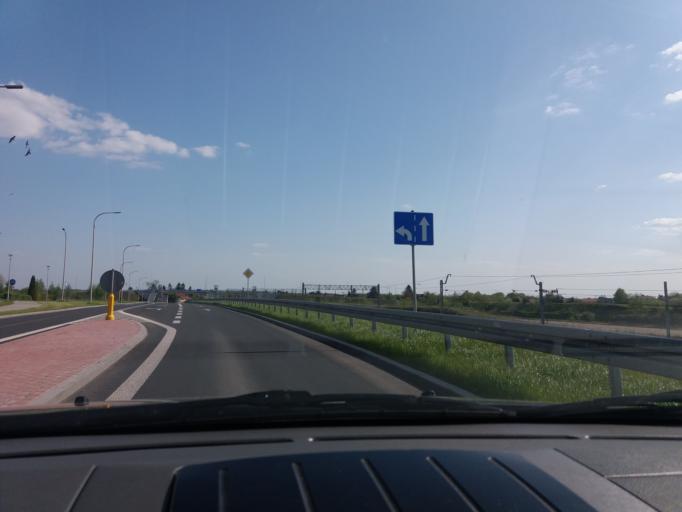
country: PL
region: Masovian Voivodeship
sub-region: Powiat mlawski
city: Mlawa
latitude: 53.1117
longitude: 20.3624
